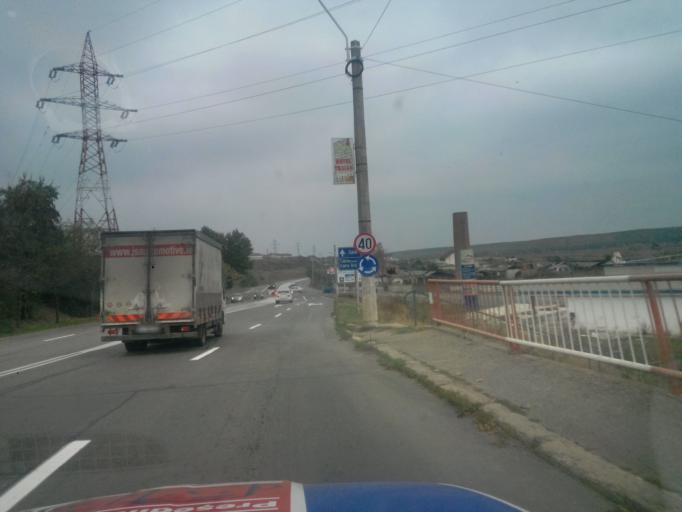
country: RO
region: Braila
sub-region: Municipiul Braila
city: Braila
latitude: 45.2902
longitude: 27.9795
